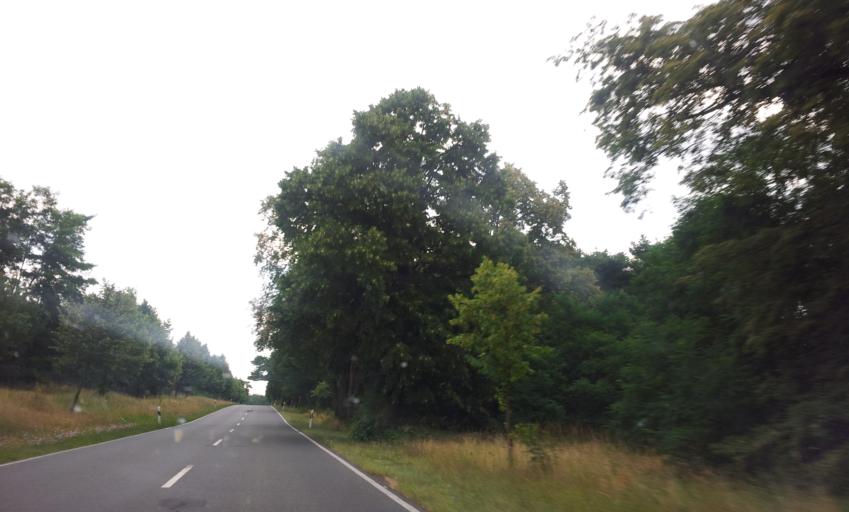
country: DE
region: Brandenburg
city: Juterbog
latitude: 52.0059
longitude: 13.0616
